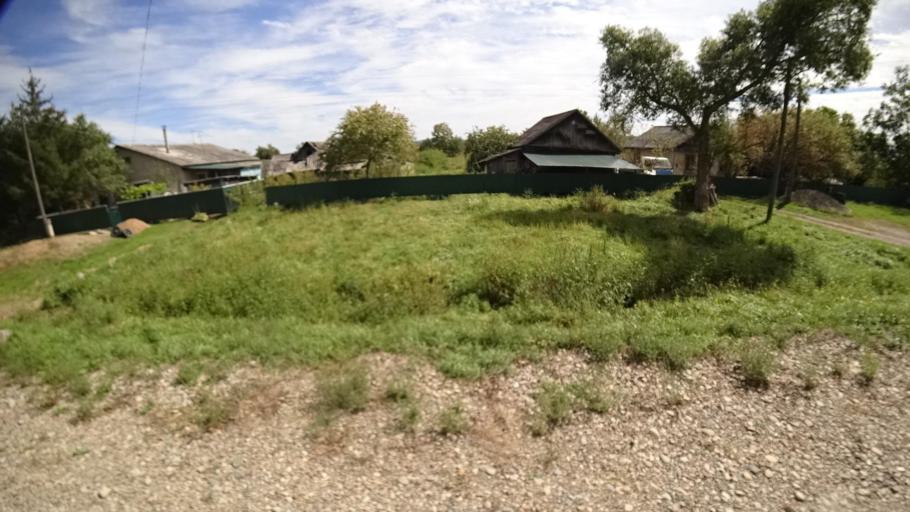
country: RU
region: Primorskiy
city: Yakovlevka
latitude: 44.6415
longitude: 133.6005
